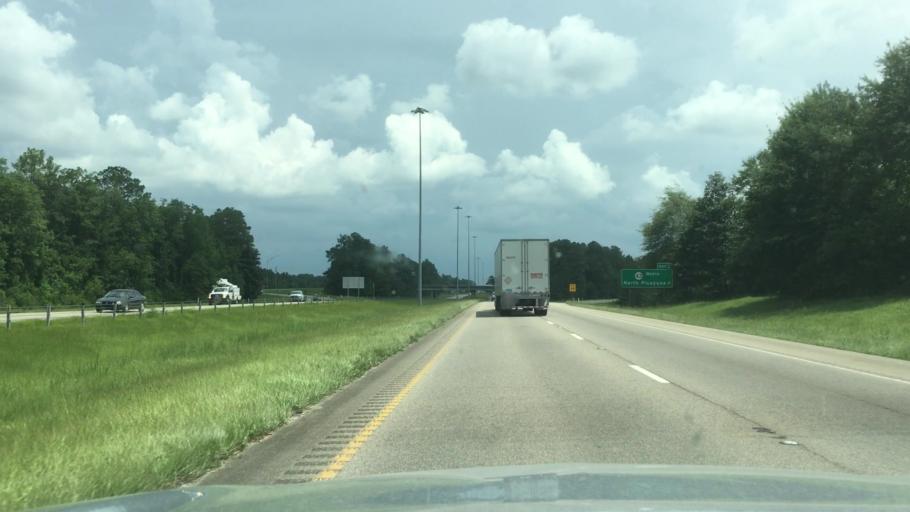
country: US
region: Mississippi
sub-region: Pearl River County
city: Picayune
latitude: 30.5388
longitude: -89.6521
